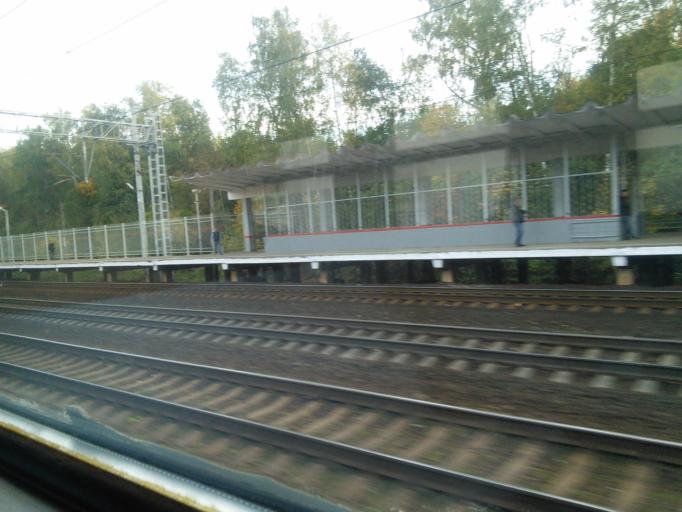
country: RU
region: Moskovskaya
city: Levoberezhnaya
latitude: 55.8870
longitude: 37.4688
